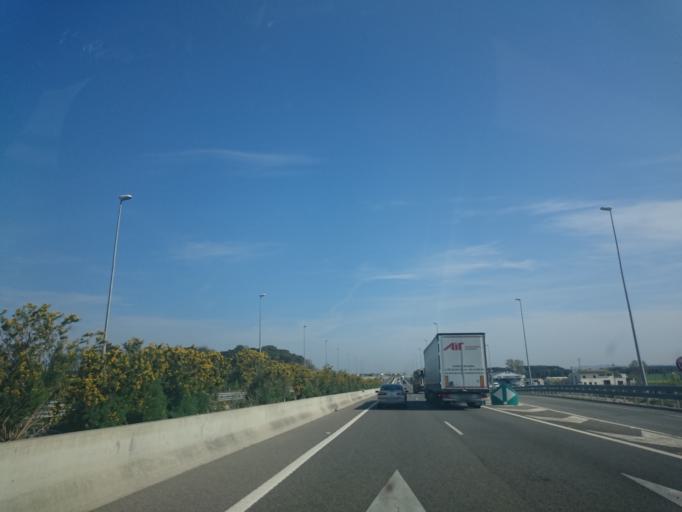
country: ES
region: Catalonia
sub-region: Provincia de Girona
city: Riudellots de la Selva
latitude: 41.8848
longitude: 2.7819
